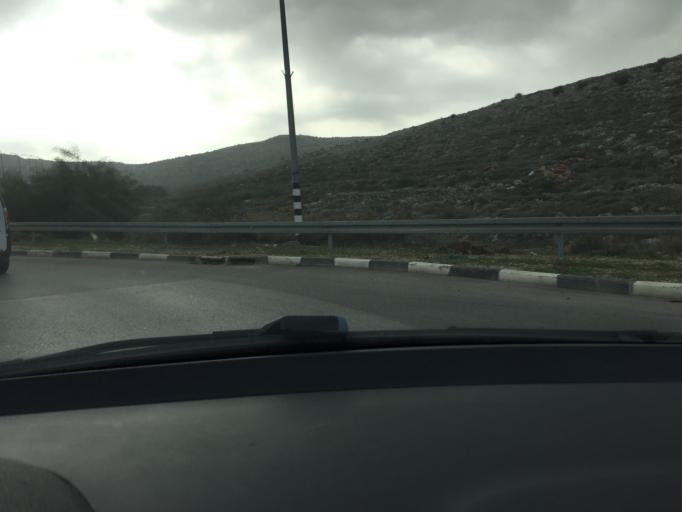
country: PS
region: West Bank
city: Al Lubban al Gharbi
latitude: 32.0330
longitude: 35.0482
